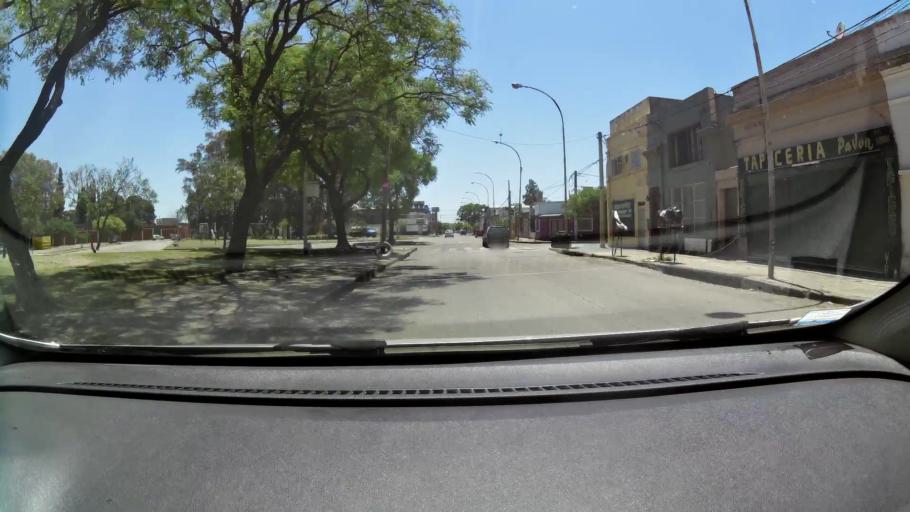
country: AR
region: Cordoba
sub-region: Departamento de Capital
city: Cordoba
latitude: -31.4011
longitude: -64.2110
